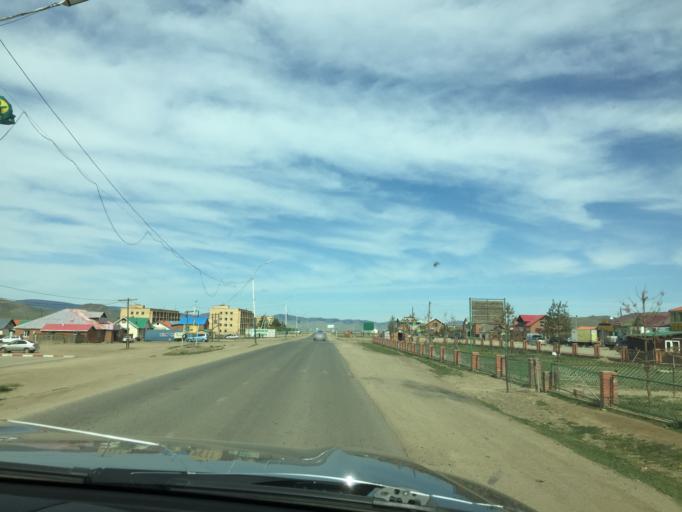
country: MN
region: Central Aimak
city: Ihsueuej
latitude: 48.2240
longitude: 106.2940
